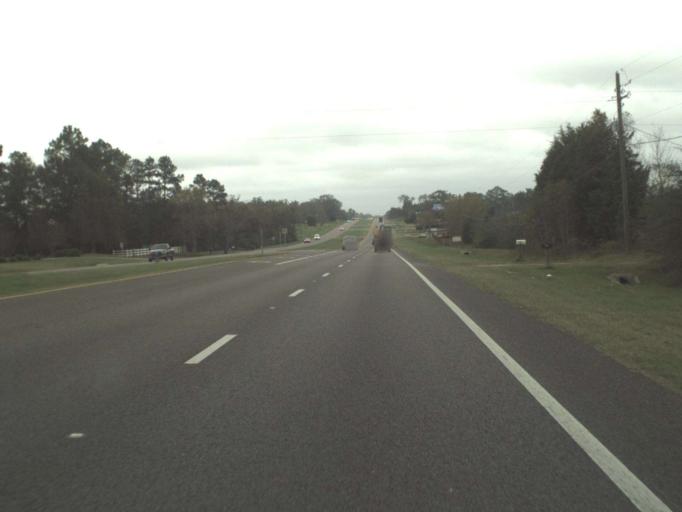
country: US
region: Florida
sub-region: Escambia County
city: Molino
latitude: 30.7026
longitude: -87.3502
